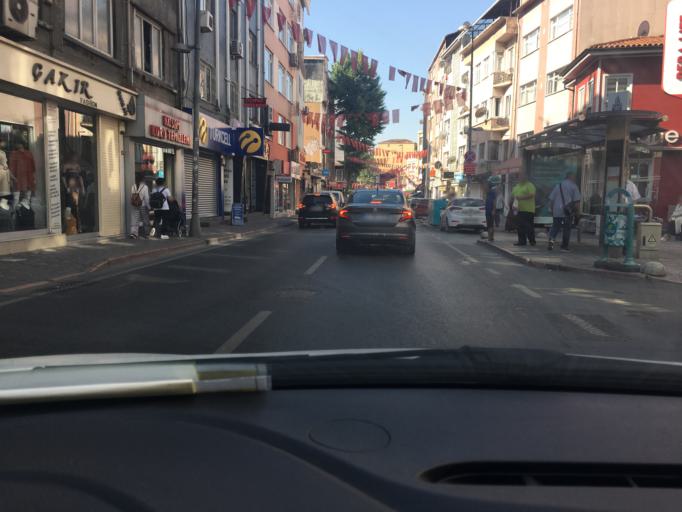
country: TR
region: Istanbul
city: Eminoenue
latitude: 41.0350
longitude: 28.9684
